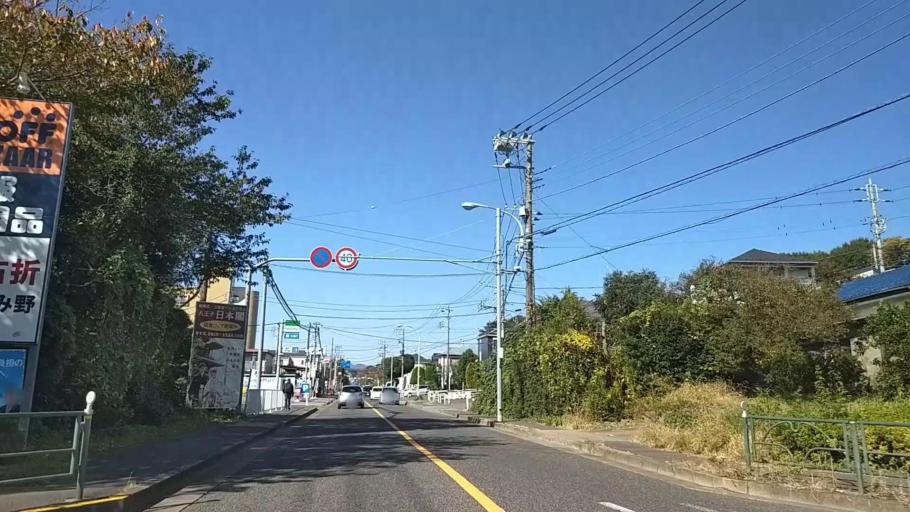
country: JP
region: Tokyo
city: Hachioji
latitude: 35.6032
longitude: 139.3478
